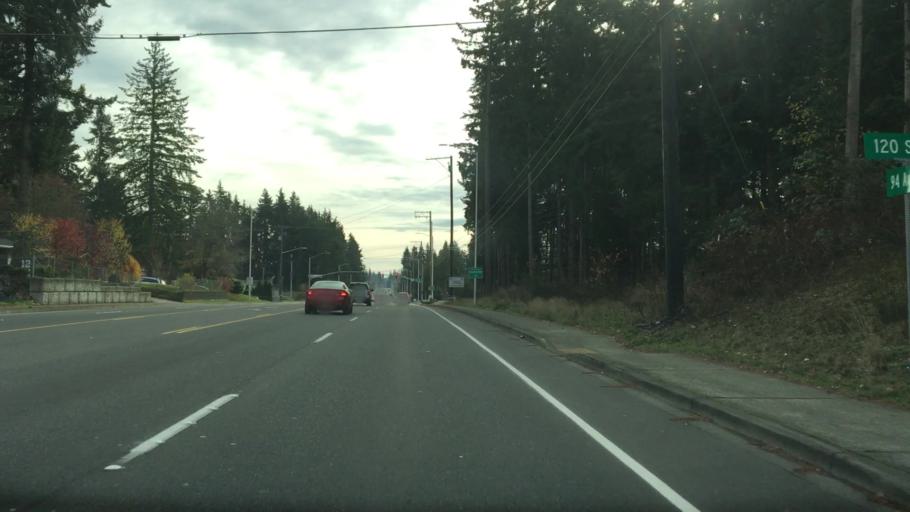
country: US
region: Washington
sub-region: Pierce County
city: South Hill
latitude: 47.1475
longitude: -122.3041
